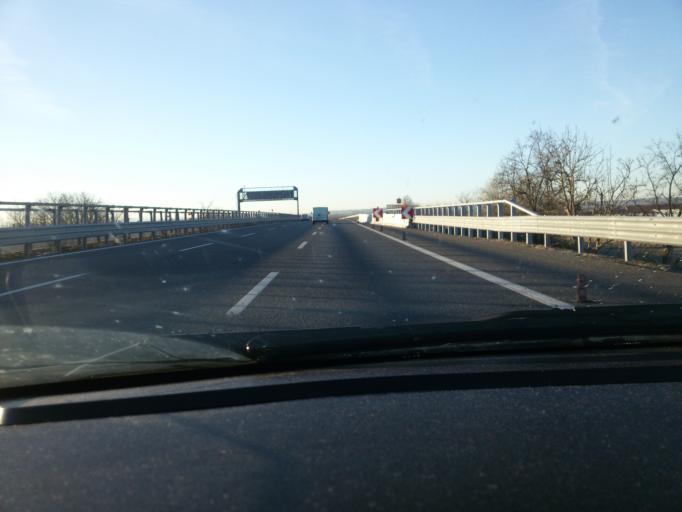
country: IT
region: Piedmont
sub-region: Provincia di Alessandria
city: Borgo San Martino
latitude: 45.1119
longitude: 8.4893
